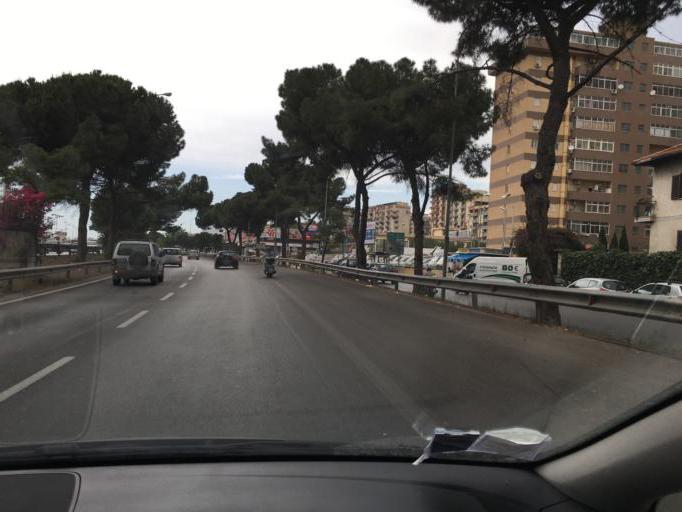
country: IT
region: Sicily
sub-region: Palermo
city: Palermo
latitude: 38.1435
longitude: 13.3310
